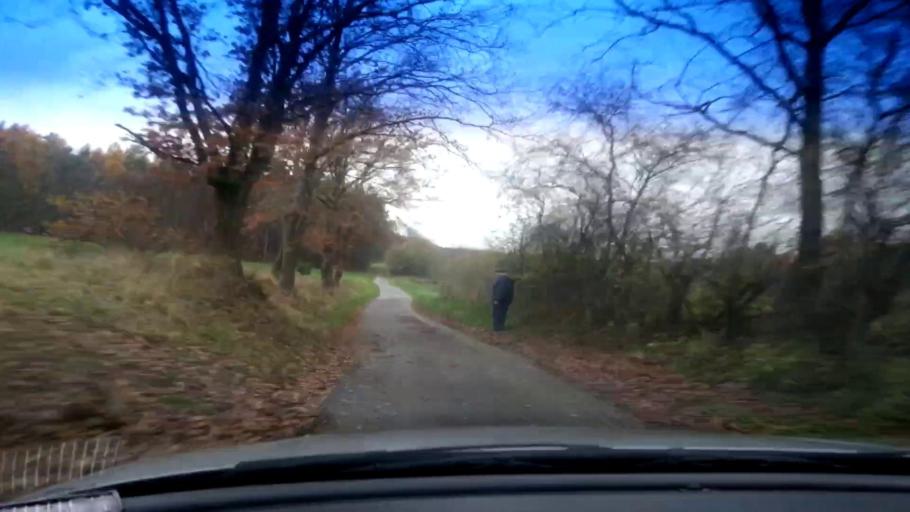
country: DE
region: Bavaria
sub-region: Upper Franconia
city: Stegaurach
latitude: 49.8572
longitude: 10.8219
